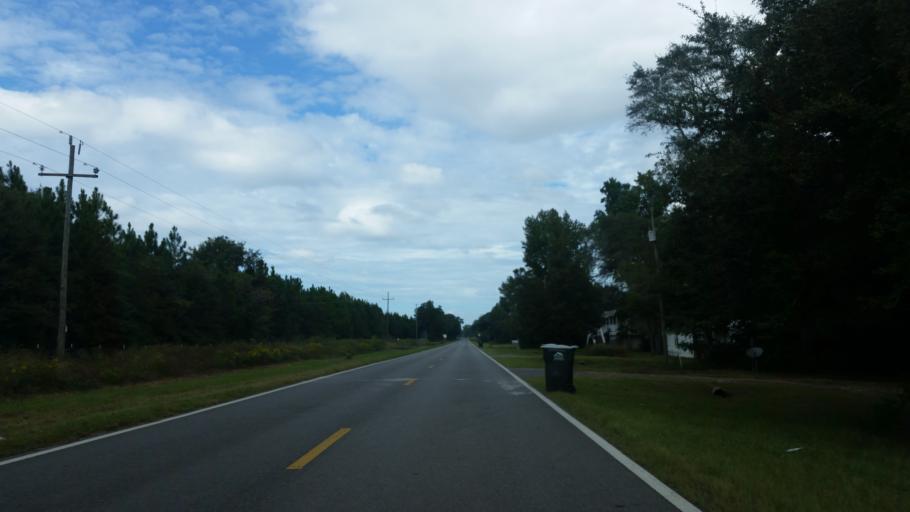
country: US
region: Florida
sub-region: Santa Rosa County
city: Point Baker
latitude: 30.6930
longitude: -86.9933
